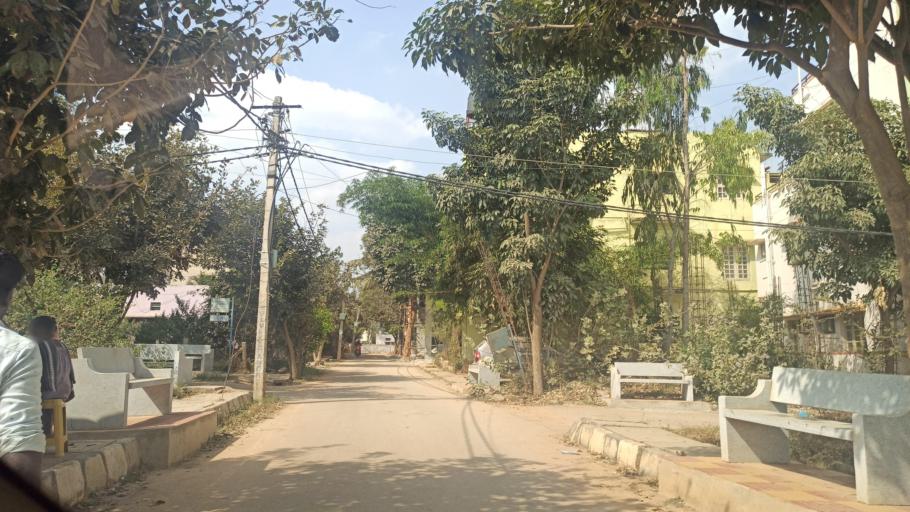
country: IN
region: Karnataka
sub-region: Bangalore Urban
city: Yelahanka
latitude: 13.1133
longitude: 77.6098
